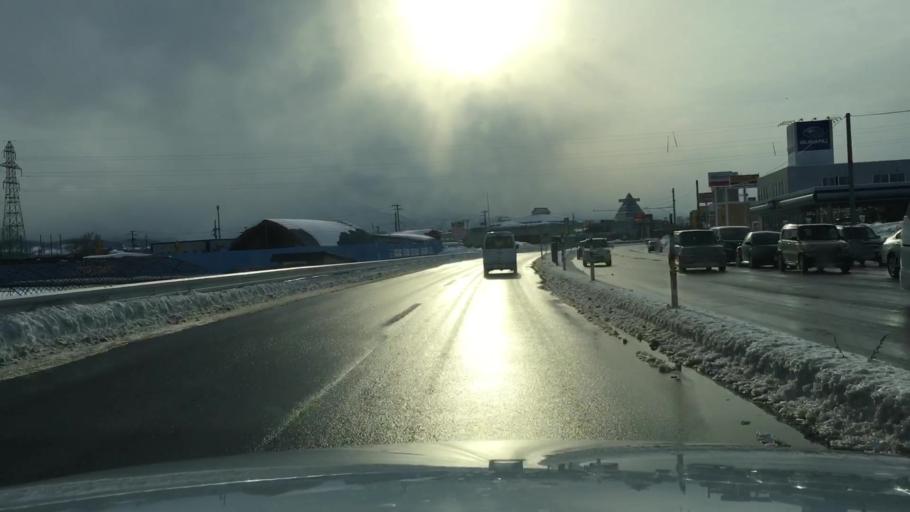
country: JP
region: Aomori
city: Hirosaki
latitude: 40.5985
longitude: 140.5134
